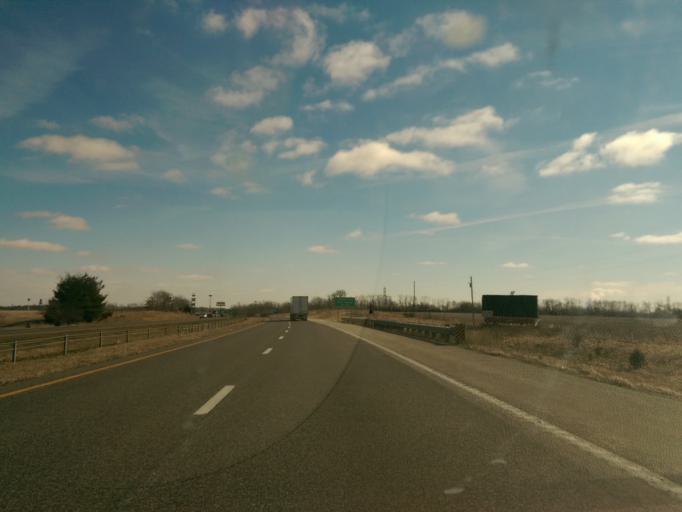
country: US
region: Missouri
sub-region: Callaway County
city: Fulton
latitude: 38.9468
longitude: -91.9552
